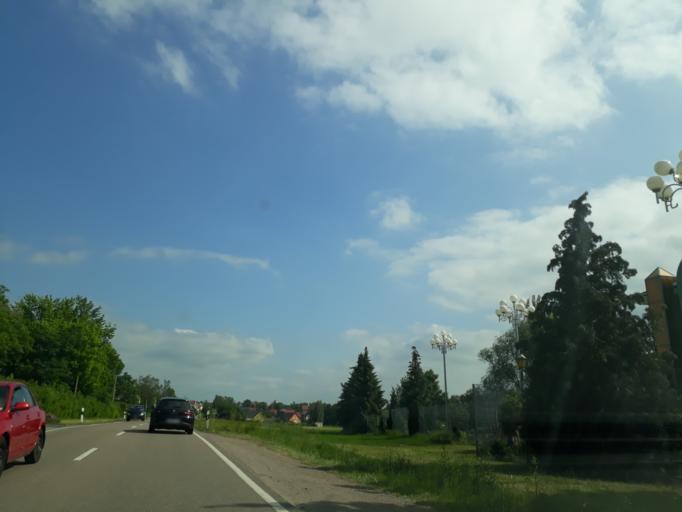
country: DE
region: Saxony
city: Wilsdruff
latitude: 51.0390
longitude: 13.5445
